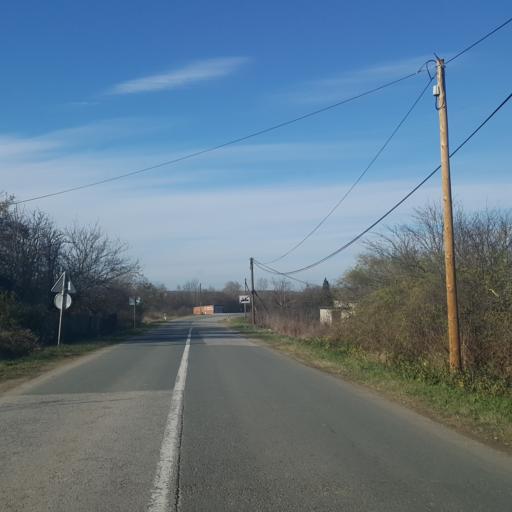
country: RS
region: Central Serbia
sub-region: Sumadijski Okrug
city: Raca
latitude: 44.2414
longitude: 20.8324
